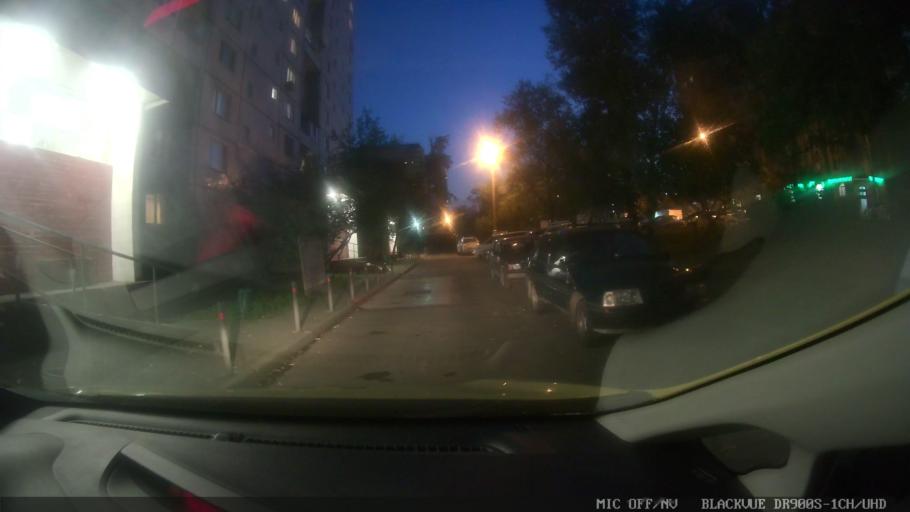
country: RU
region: Moskovskaya
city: Vostochnoe Degunino
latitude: 55.8742
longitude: 37.5615
